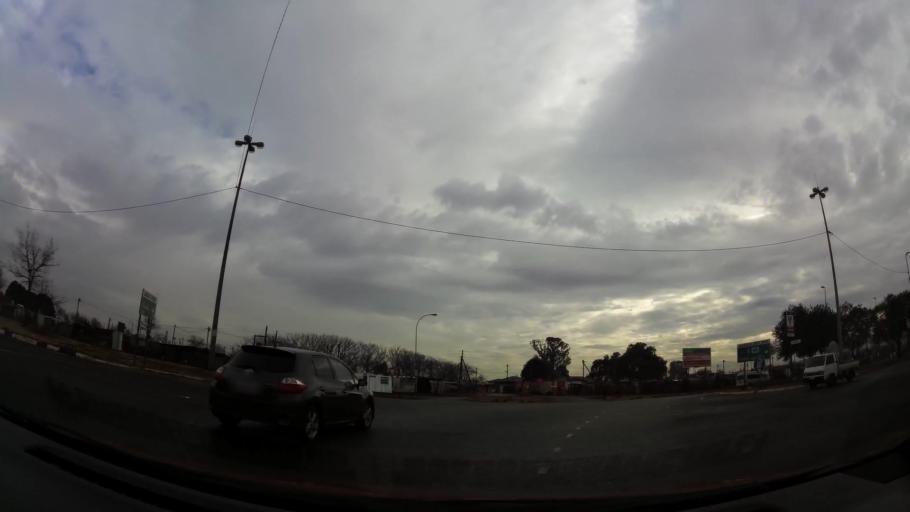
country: ZA
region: Gauteng
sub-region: City of Johannesburg Metropolitan Municipality
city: Soweto
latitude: -26.2906
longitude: 27.8443
